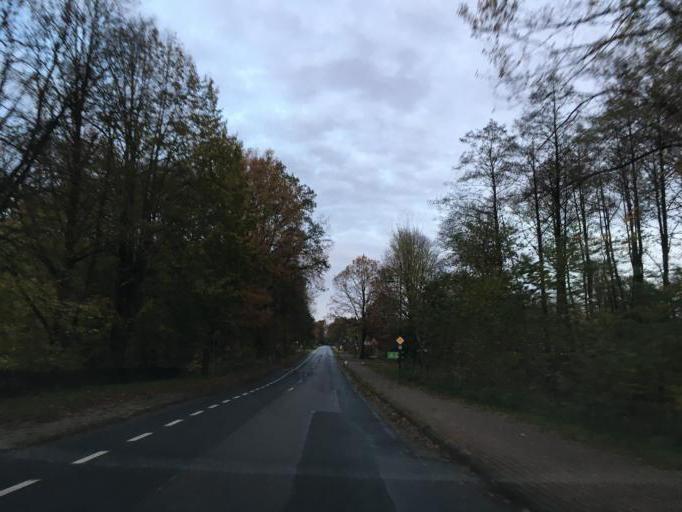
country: DE
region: Lower Saxony
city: Bispingen
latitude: 53.0881
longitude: 9.9980
